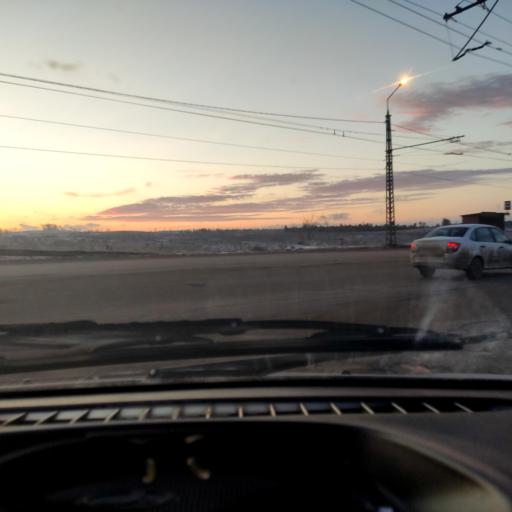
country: RU
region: Samara
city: Zhigulevsk
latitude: 53.5138
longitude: 49.5306
